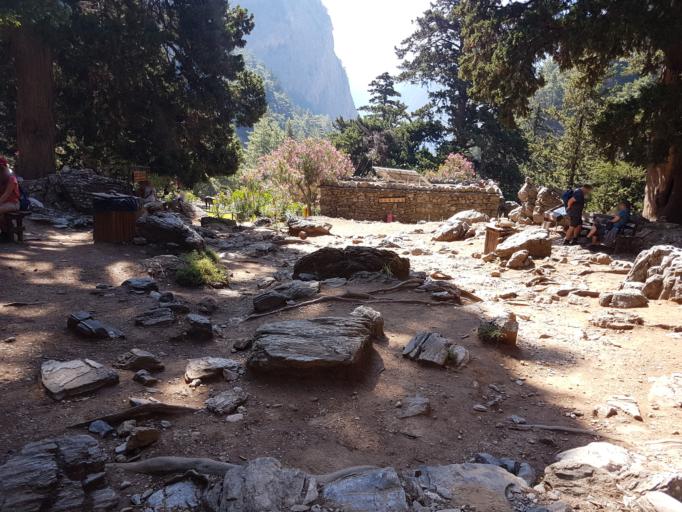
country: GR
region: Crete
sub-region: Nomos Chanias
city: Perivolia
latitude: 35.3068
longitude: 23.9360
